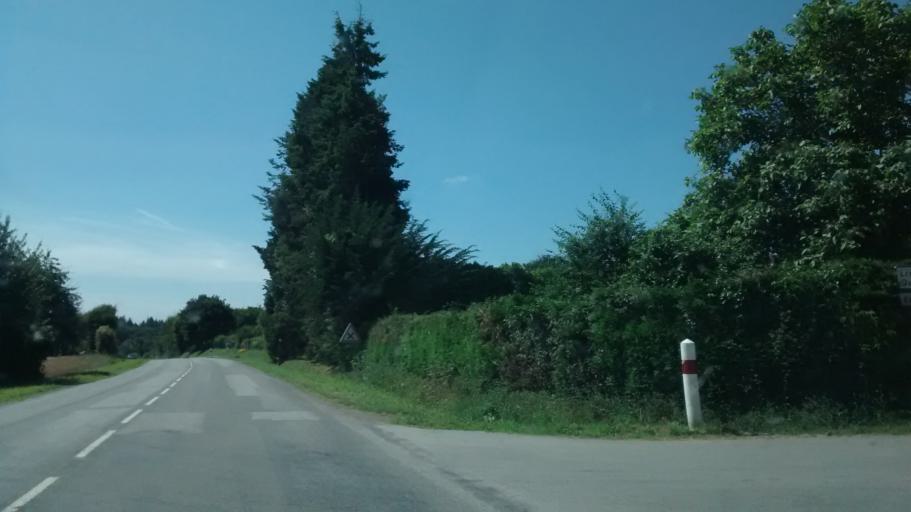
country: FR
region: Brittany
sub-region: Departement du Morbihan
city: Campeneac
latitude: 47.9447
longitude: -2.2861
